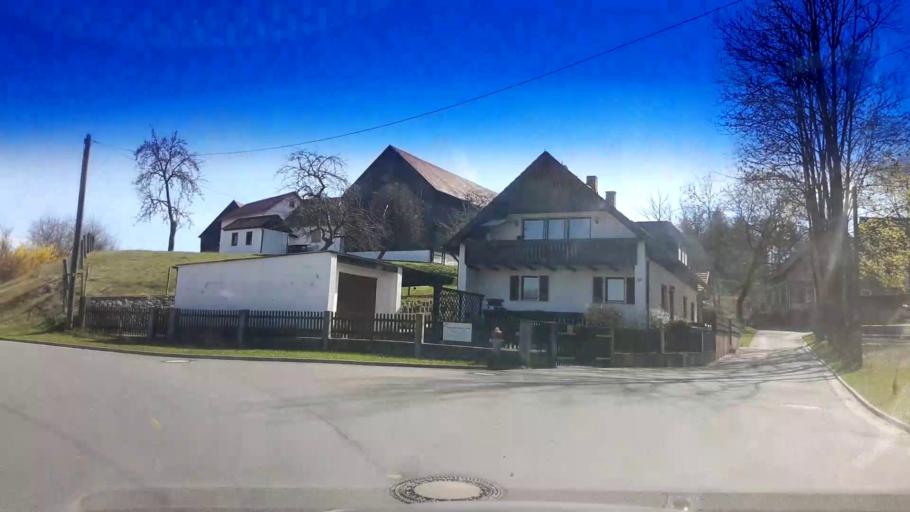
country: DE
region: Bavaria
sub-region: Upper Franconia
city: Bindlach
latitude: 50.0104
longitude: 11.6234
